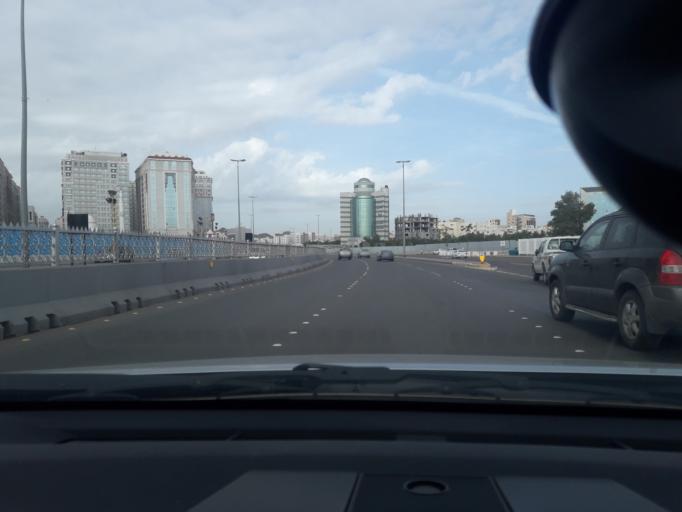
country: SA
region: Al Madinah al Munawwarah
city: Medina
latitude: 24.4727
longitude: 39.6170
